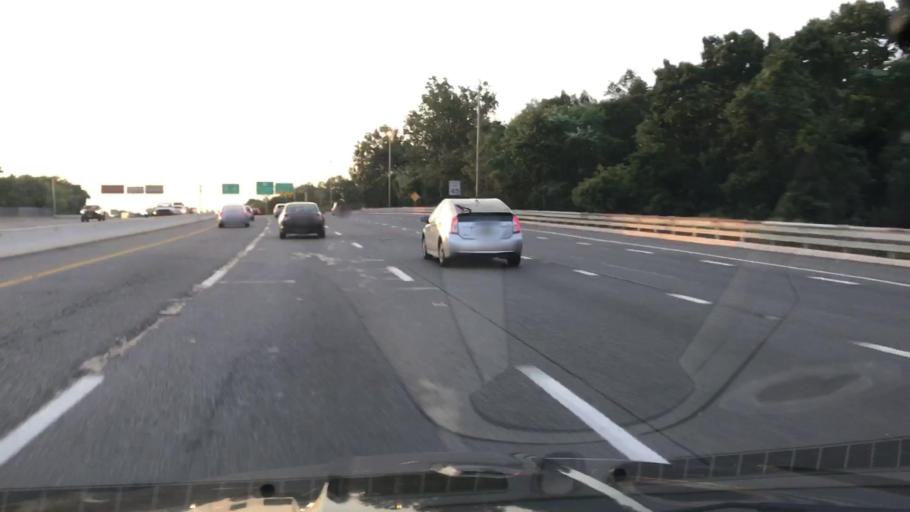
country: US
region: New Jersey
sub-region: Camden County
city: Pennsauken
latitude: 39.9751
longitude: -75.0457
